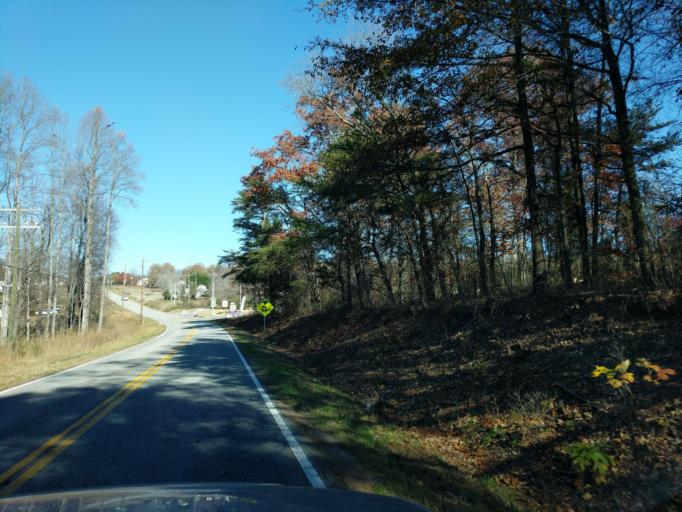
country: US
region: South Carolina
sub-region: Spartanburg County
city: Inman Mills
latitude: 35.0466
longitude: -82.1811
